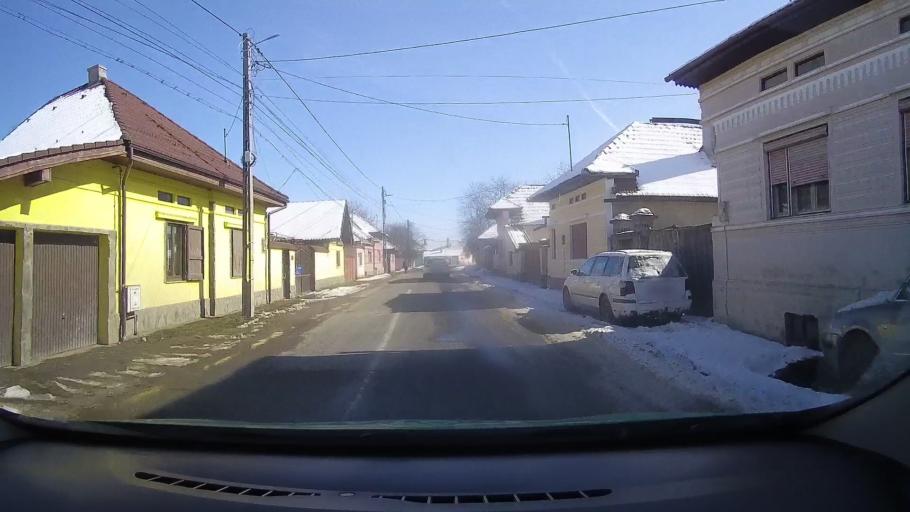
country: RO
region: Brasov
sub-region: Comuna Recea
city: Recea
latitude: 45.7331
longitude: 24.9377
